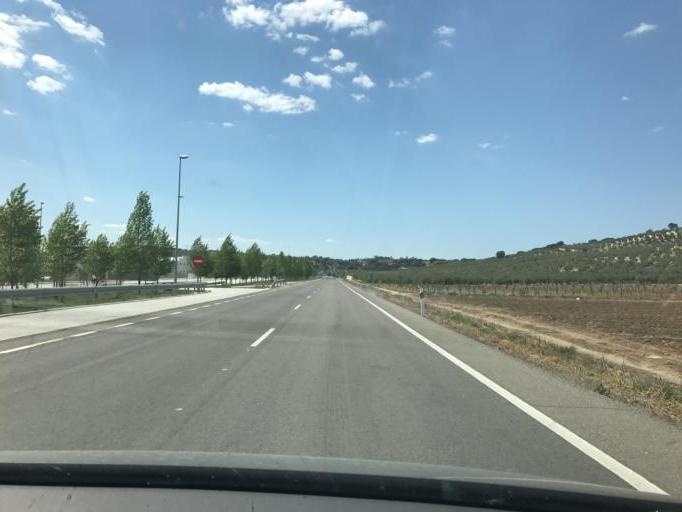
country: ES
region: Andalusia
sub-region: Provincia de Jaen
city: Alcala la Real
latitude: 37.4521
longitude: -3.8787
